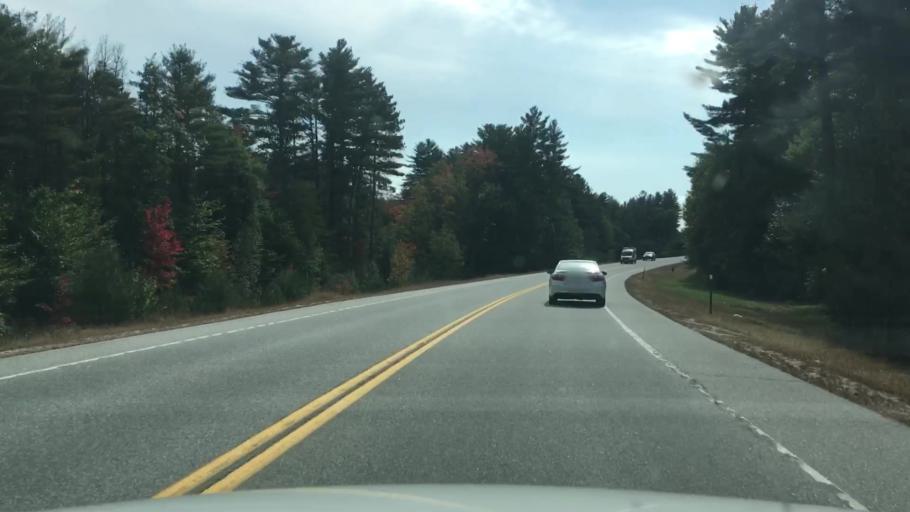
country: US
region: New Hampshire
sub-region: Carroll County
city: North Conway
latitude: 44.0391
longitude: -71.1162
